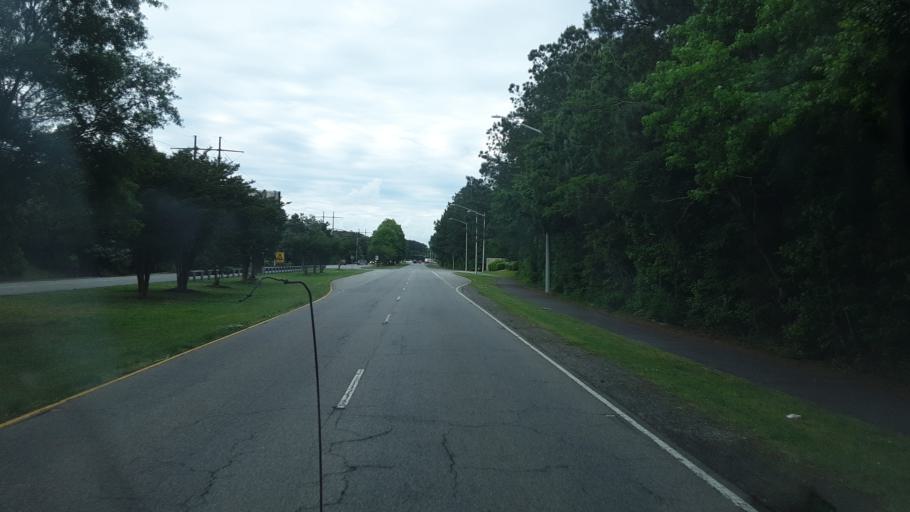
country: US
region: Virginia
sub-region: City of Virginia Beach
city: Virginia Beach
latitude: 36.7990
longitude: -75.9938
